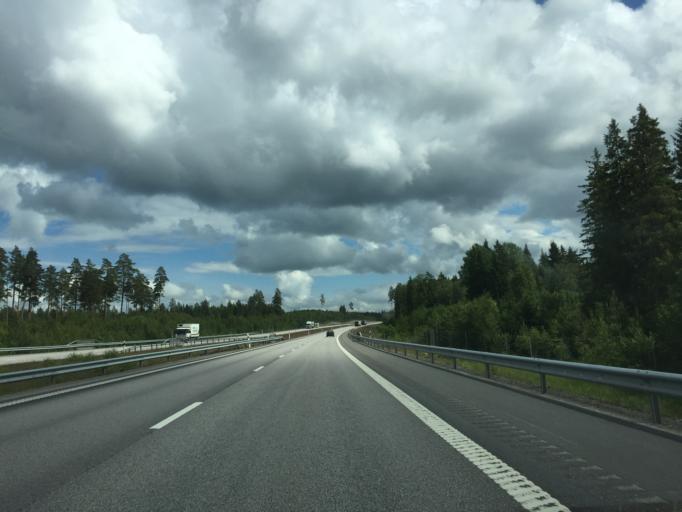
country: SE
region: OErebro
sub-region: Lindesbergs Kommun
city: Fellingsbro
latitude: 59.3725
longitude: 15.5904
